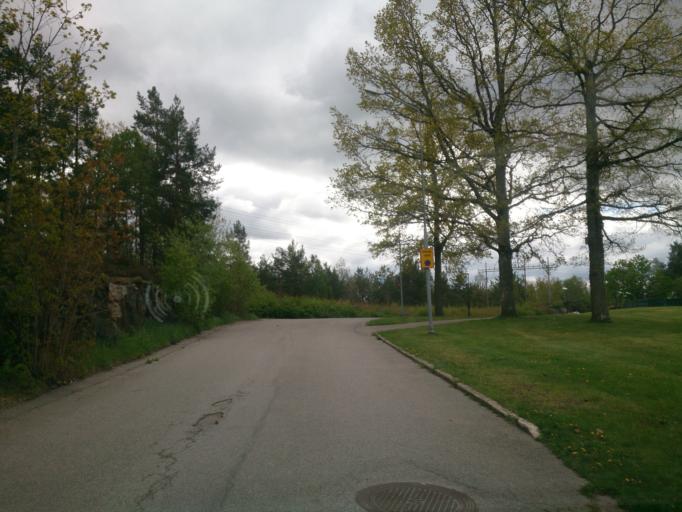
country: SE
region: OEstergoetland
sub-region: Atvidabergs Kommun
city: Atvidaberg
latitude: 58.2071
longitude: 16.0150
